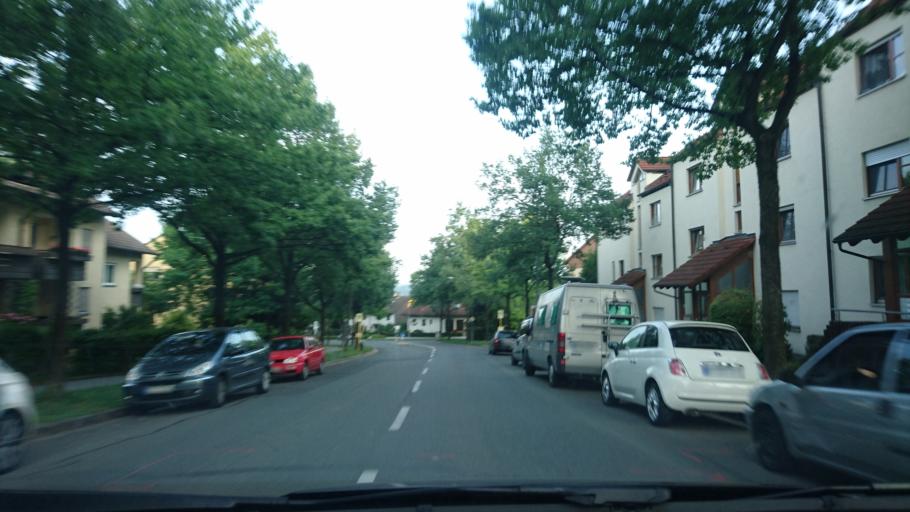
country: DE
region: Bavaria
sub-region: Upper Franconia
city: Heinersreuth
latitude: 49.9441
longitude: 11.5384
